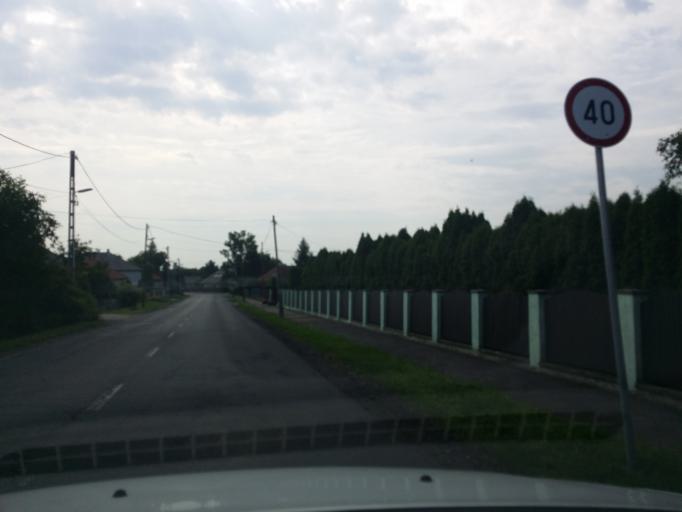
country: HU
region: Borsod-Abauj-Zemplen
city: Satoraljaujhely
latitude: 48.4662
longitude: 21.5887
